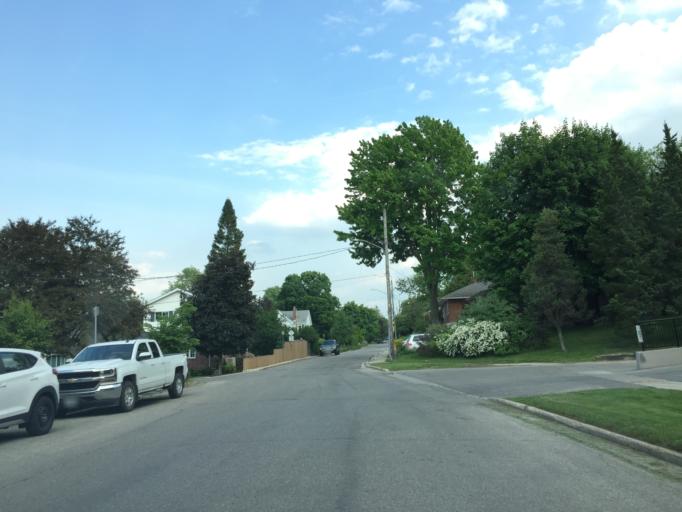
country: CA
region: Ontario
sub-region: Wellington County
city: Guelph
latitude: 43.5547
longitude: -80.2715
